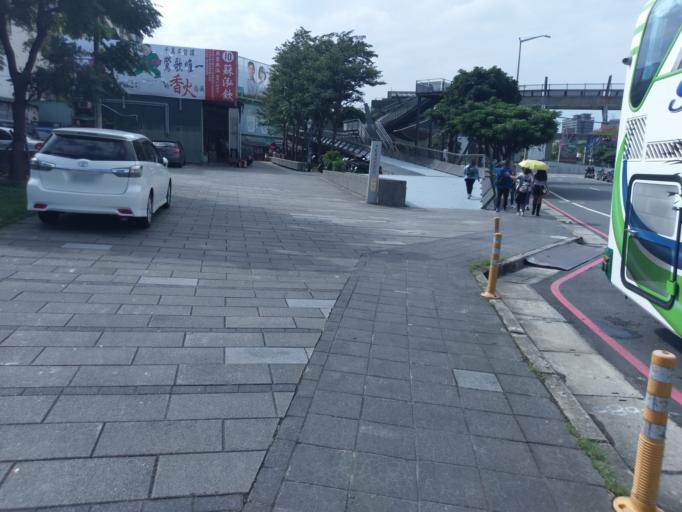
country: TW
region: Taiwan
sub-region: Taoyuan
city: Taoyuan
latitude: 24.9499
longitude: 121.3537
